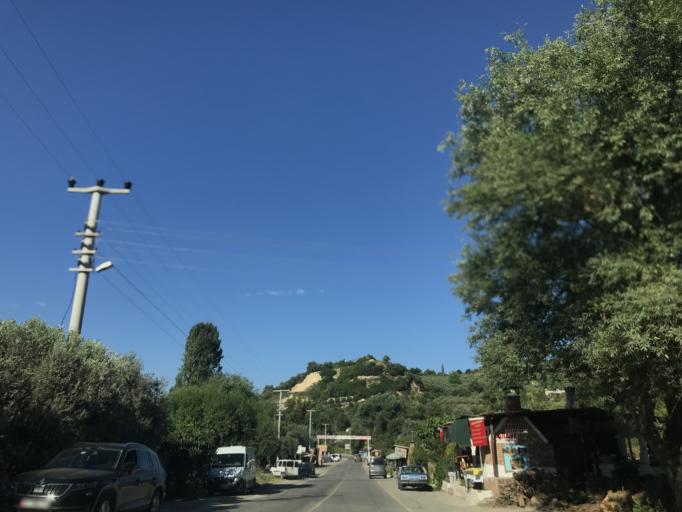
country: TR
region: Aydin
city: Davutlar
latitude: 37.7399
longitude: 27.3428
